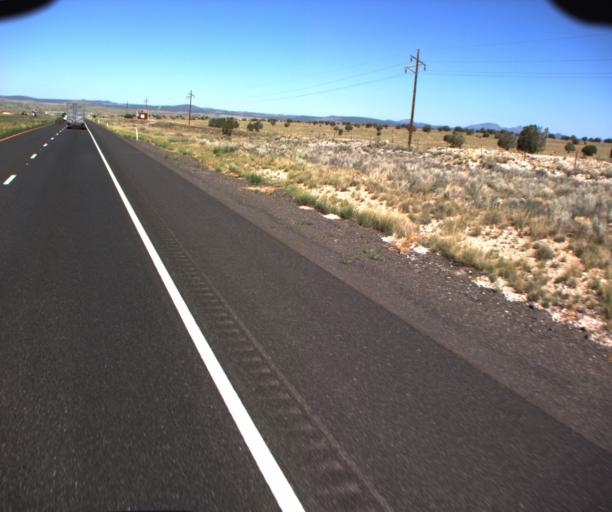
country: US
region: Arizona
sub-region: Yavapai County
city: Paulden
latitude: 35.2270
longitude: -112.5720
